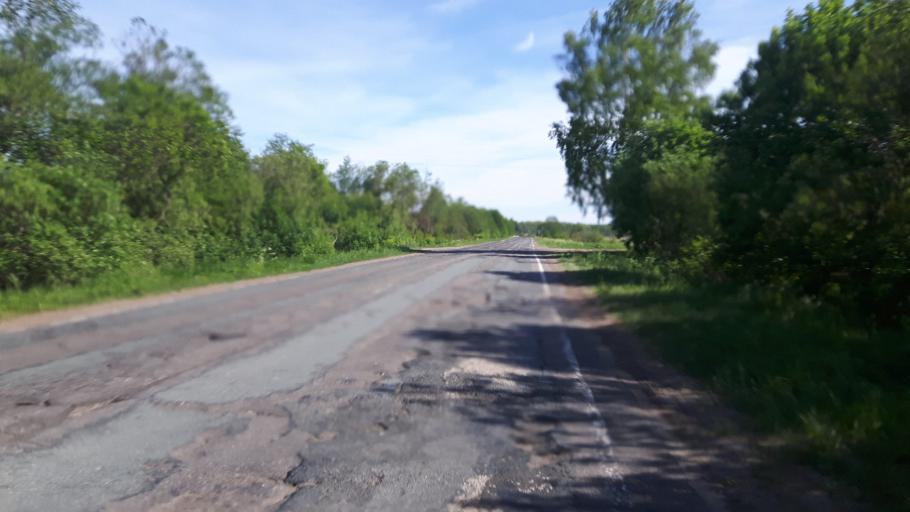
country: RU
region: Leningrad
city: Ivangorod
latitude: 59.4194
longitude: 28.3222
